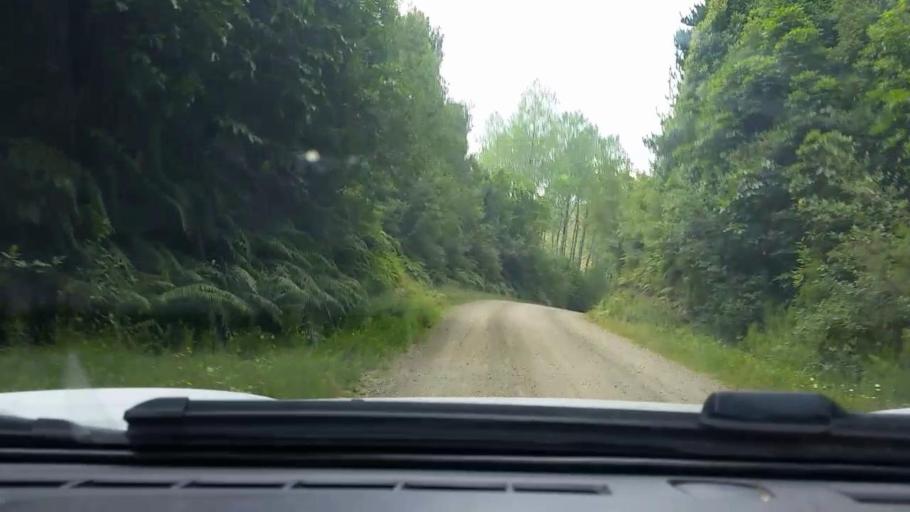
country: NZ
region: Bay of Plenty
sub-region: Kawerau District
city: Kawerau
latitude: -38.0025
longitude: 176.5983
